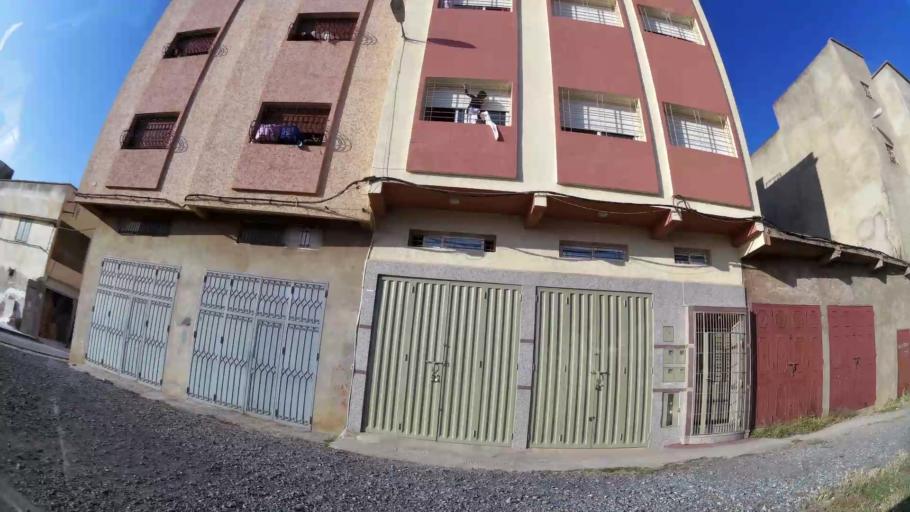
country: MA
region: Rabat-Sale-Zemmour-Zaer
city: Sale
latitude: 34.0563
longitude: -6.7879
